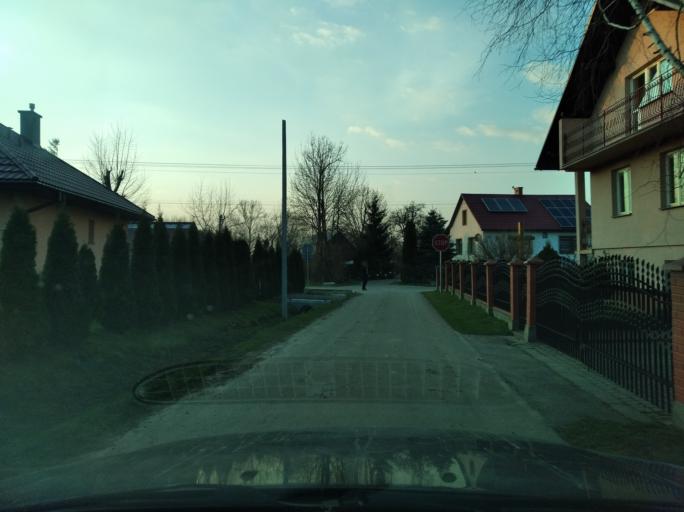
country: PL
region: Subcarpathian Voivodeship
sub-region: Powiat przeworski
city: Zurawiczki
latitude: 50.0082
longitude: 22.4879
